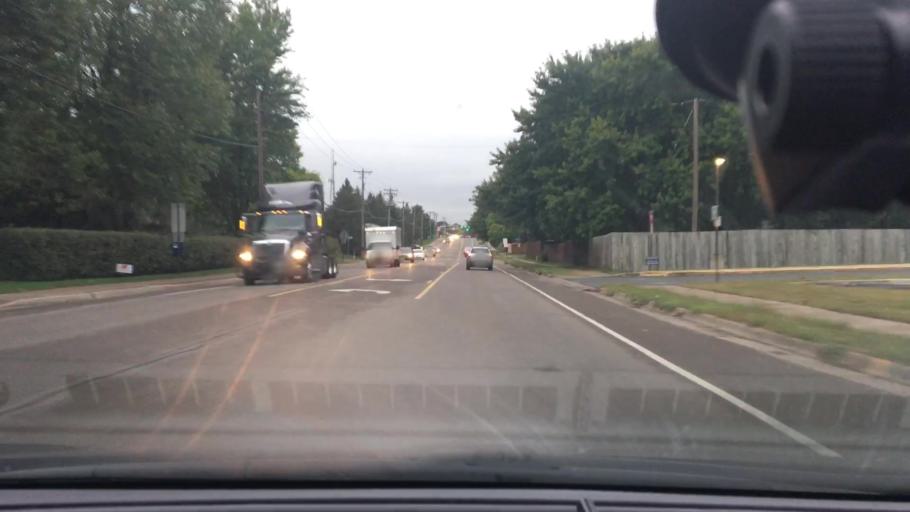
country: US
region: Minnesota
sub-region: Hennepin County
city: New Hope
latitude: 45.0075
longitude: -93.3925
